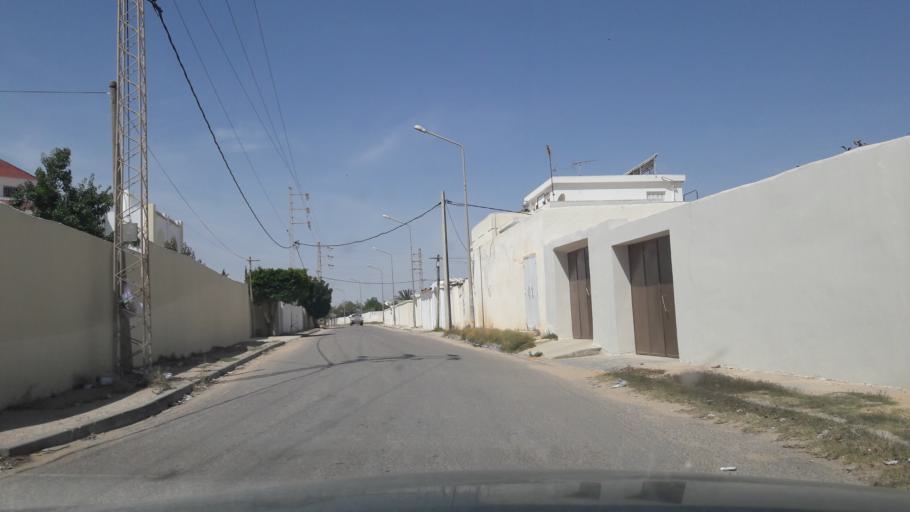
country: TN
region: Safaqis
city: Al Qarmadah
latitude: 34.7916
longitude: 10.7598
